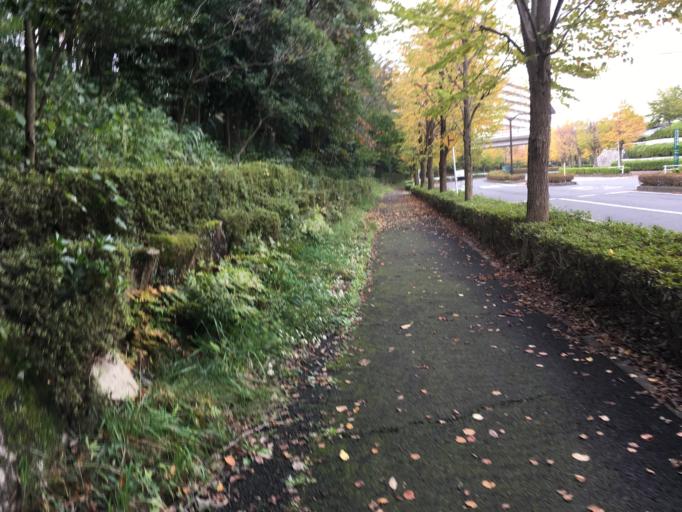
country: JP
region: Tokyo
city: Hino
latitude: 35.6107
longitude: 139.3810
